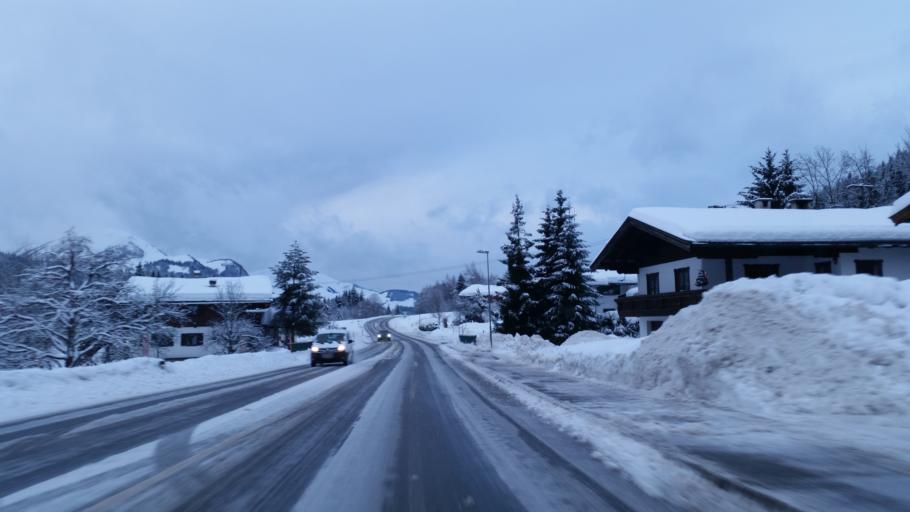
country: AT
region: Tyrol
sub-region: Politischer Bezirk Kitzbuhel
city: Hochfilzen
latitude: 47.4648
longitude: 12.5991
